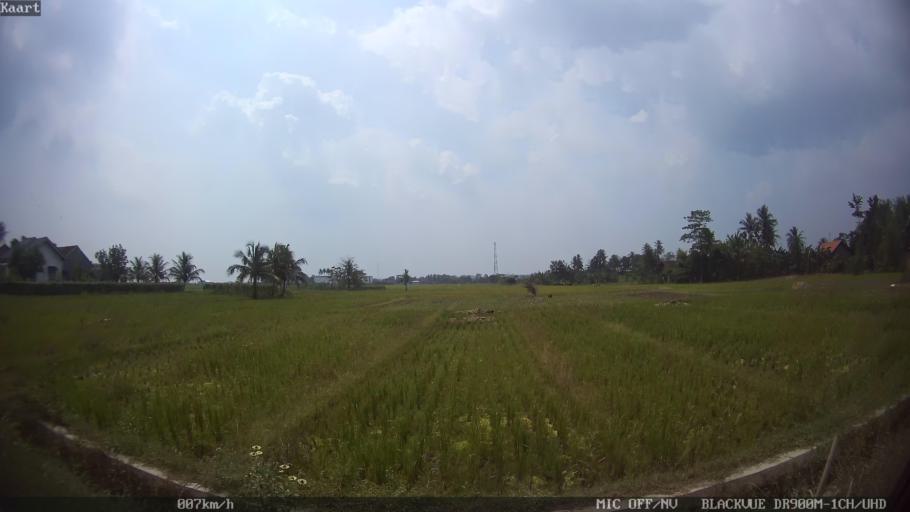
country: ID
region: Lampung
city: Gadingrejo
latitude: -5.3786
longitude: 105.0505
